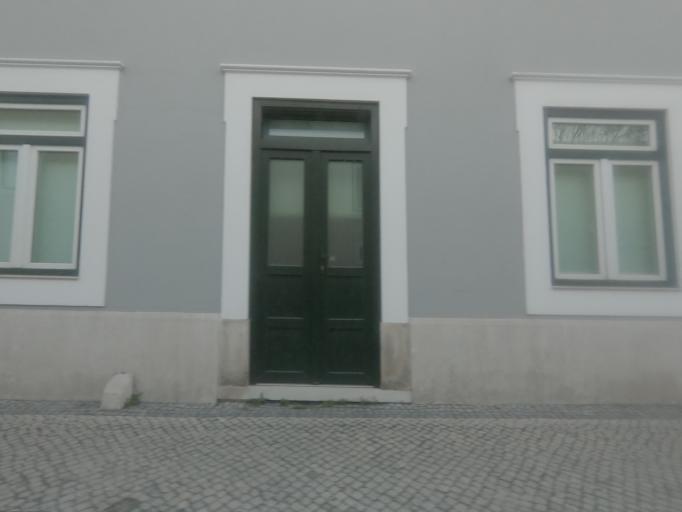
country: PT
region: Leiria
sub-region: Marinha Grande
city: Marinha Grande
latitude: 39.7500
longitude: -8.9333
